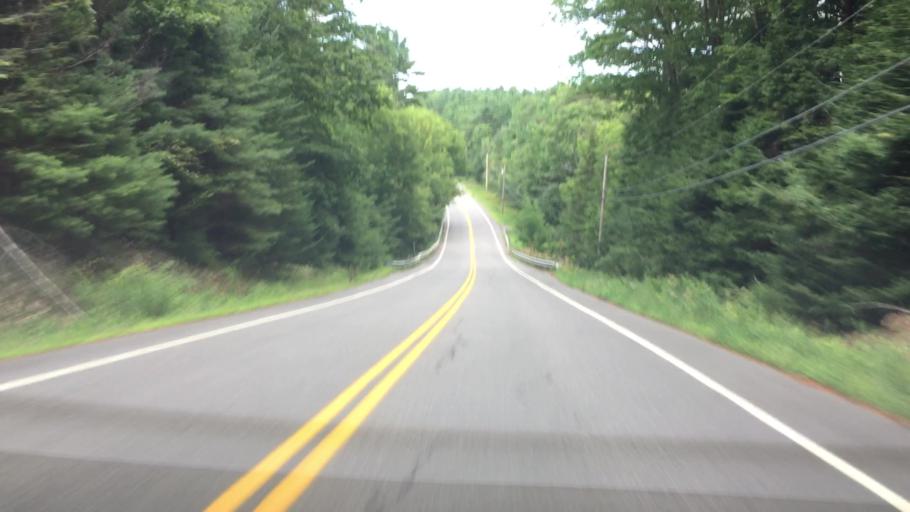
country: US
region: Maine
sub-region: Waldo County
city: Lincolnville
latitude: 44.3285
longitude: -69.0617
